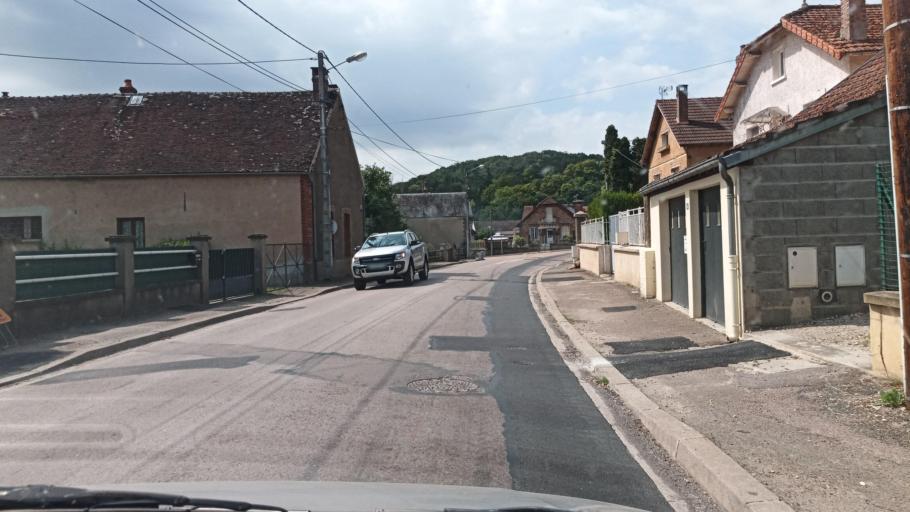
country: FR
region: Bourgogne
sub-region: Departement de l'Yonne
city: Villeneuve-sur-Yonne
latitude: 48.0796
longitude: 3.2848
